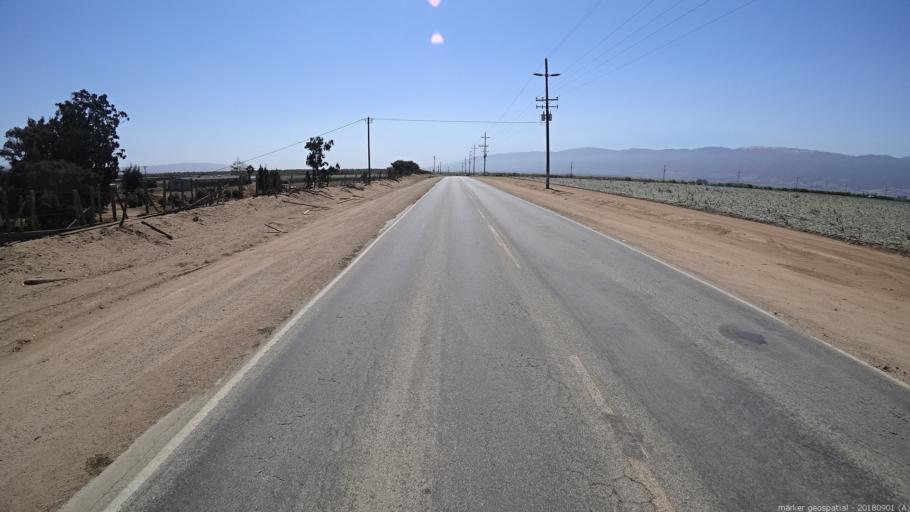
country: US
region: California
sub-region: Monterey County
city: Chualar
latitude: 36.5838
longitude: -121.4992
